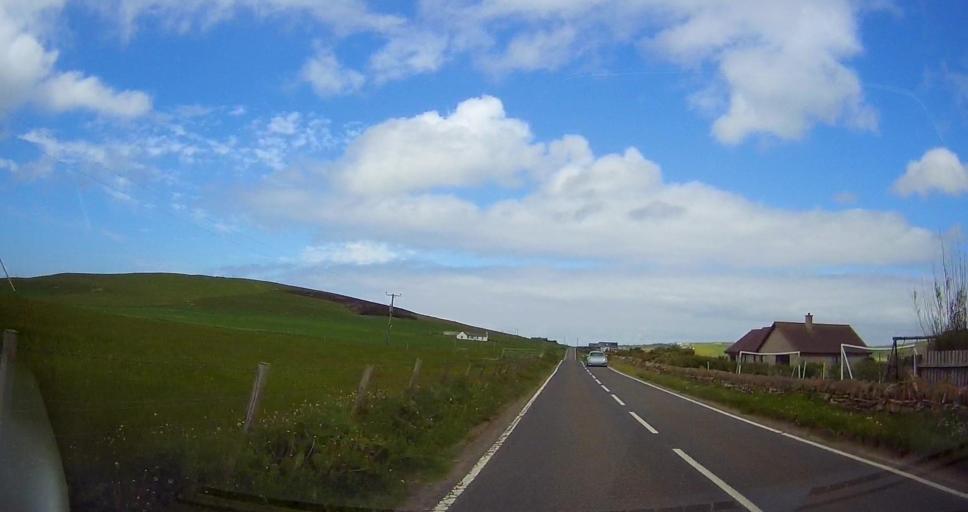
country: GB
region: Scotland
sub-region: Orkney Islands
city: Stromness
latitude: 59.1019
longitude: -3.2805
